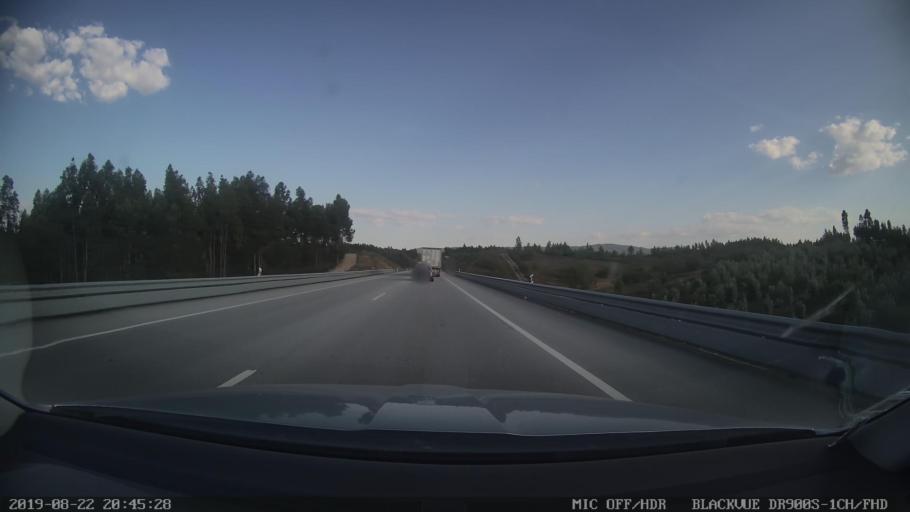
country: PT
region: Castelo Branco
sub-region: Proenca-A-Nova
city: Proenca-a-Nova
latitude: 39.7160
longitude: -7.8658
